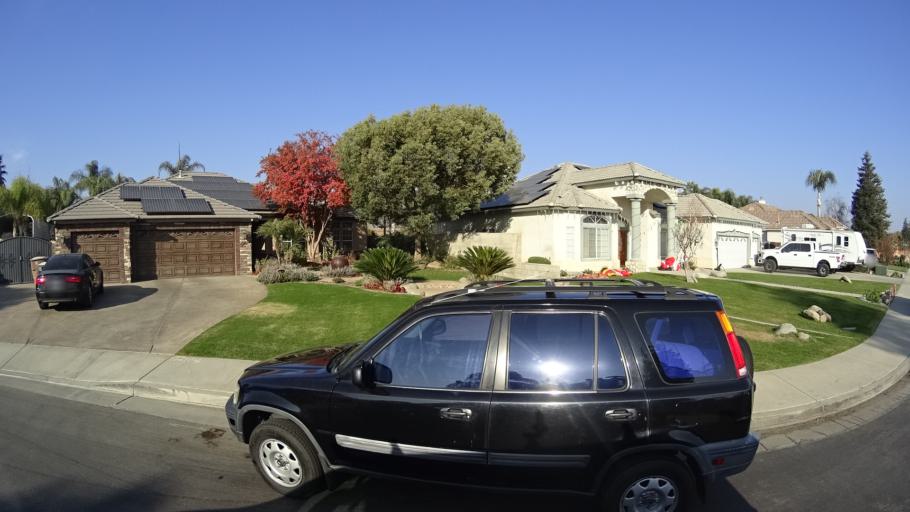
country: US
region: California
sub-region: Kern County
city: Rosedale
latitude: 35.3585
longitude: -119.1623
